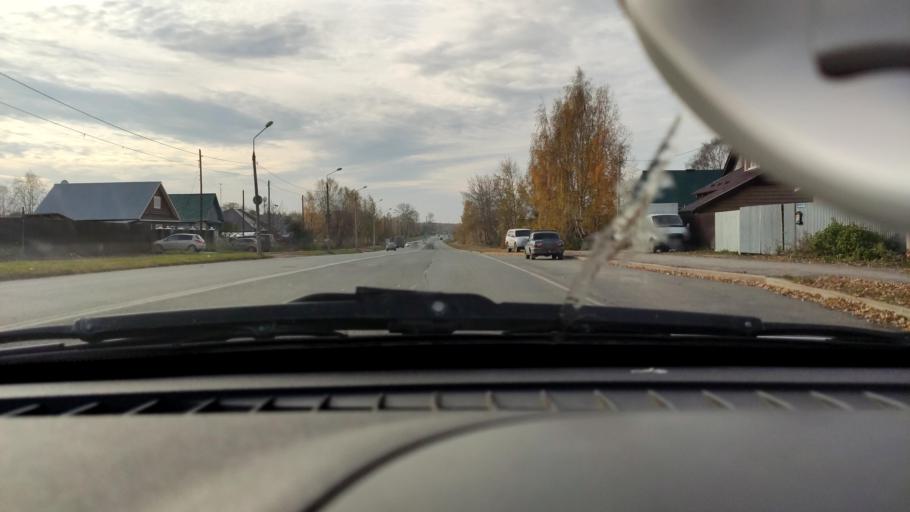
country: RU
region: Perm
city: Polazna
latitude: 58.1230
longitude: 56.4041
